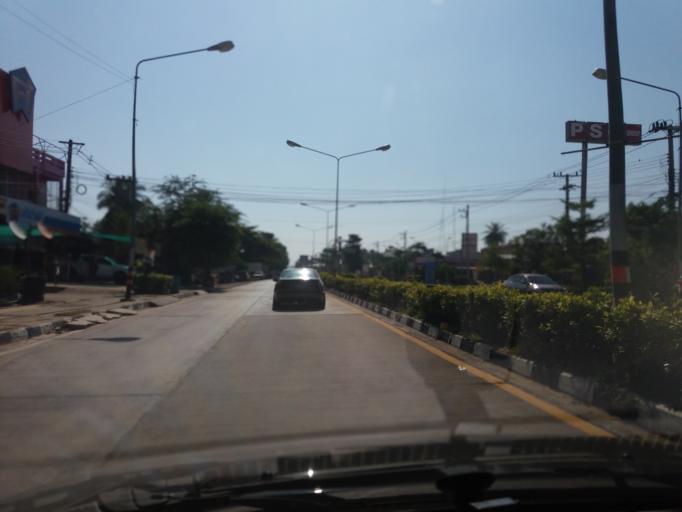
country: TH
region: Kamphaeng Phet
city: Khanu Woralaksaburi
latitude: 16.0703
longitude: 99.8631
